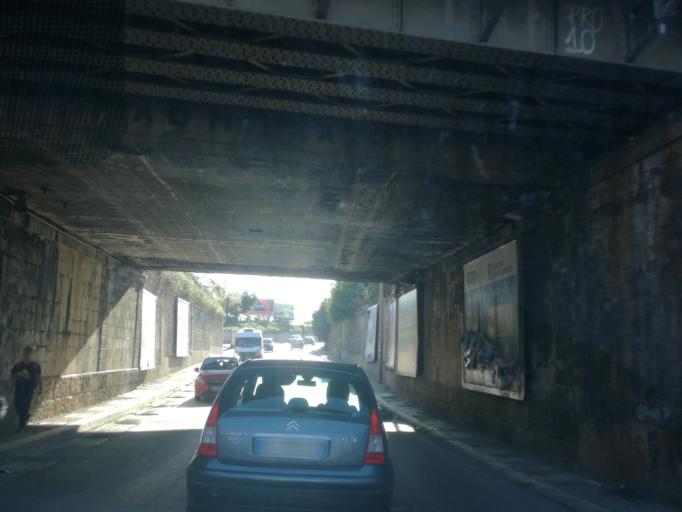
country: IT
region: Apulia
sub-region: Provincia di Bari
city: Bari
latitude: 41.1200
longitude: 16.8471
